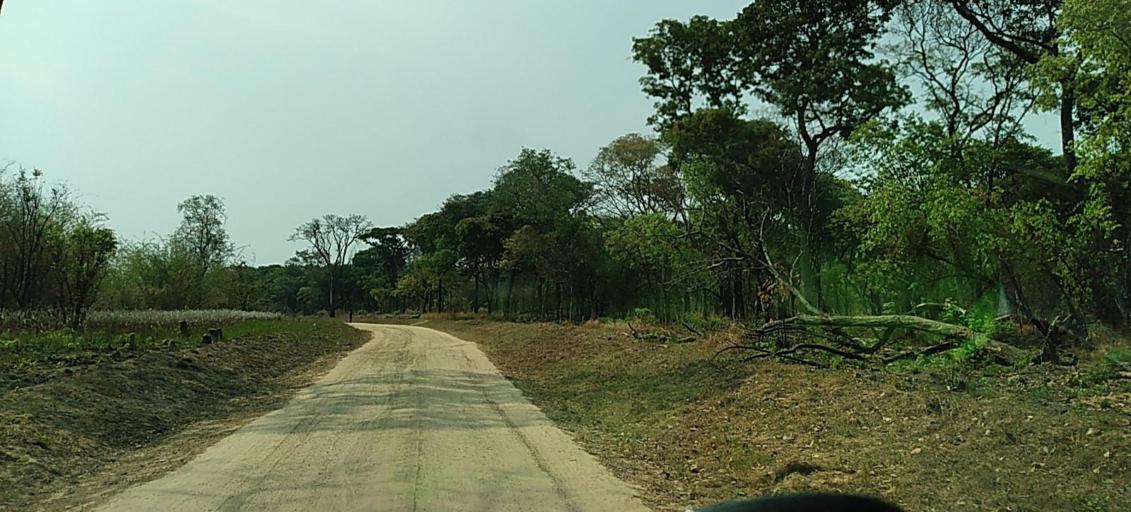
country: ZM
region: North-Western
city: Solwezi
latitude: -12.7010
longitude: 26.4143
